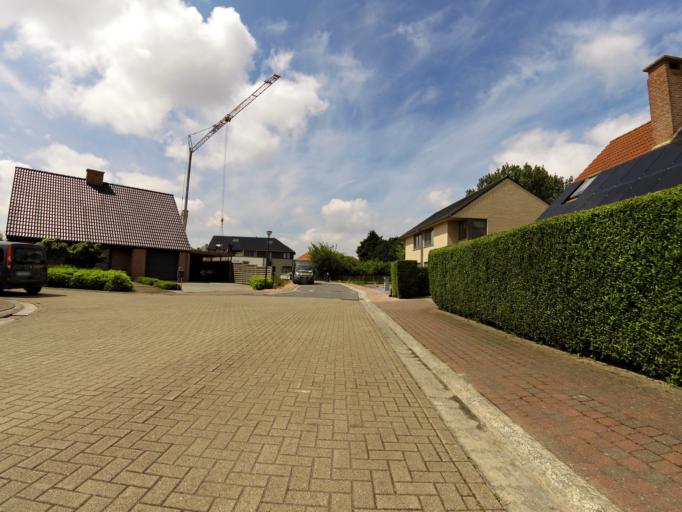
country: BE
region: Flanders
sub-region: Provincie West-Vlaanderen
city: Oudenburg
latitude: 51.2008
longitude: 2.9706
